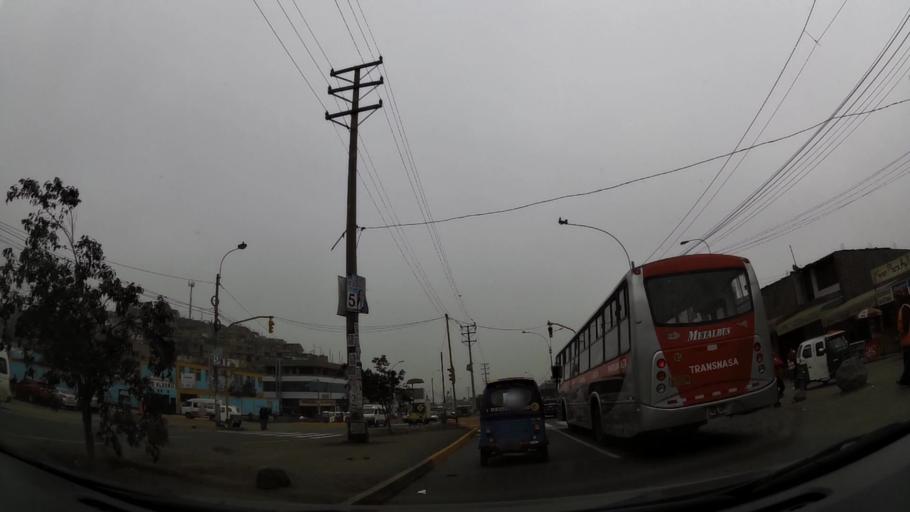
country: PE
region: Lima
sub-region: Lima
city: Urb. Santo Domingo
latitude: -11.8806
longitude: -77.0212
